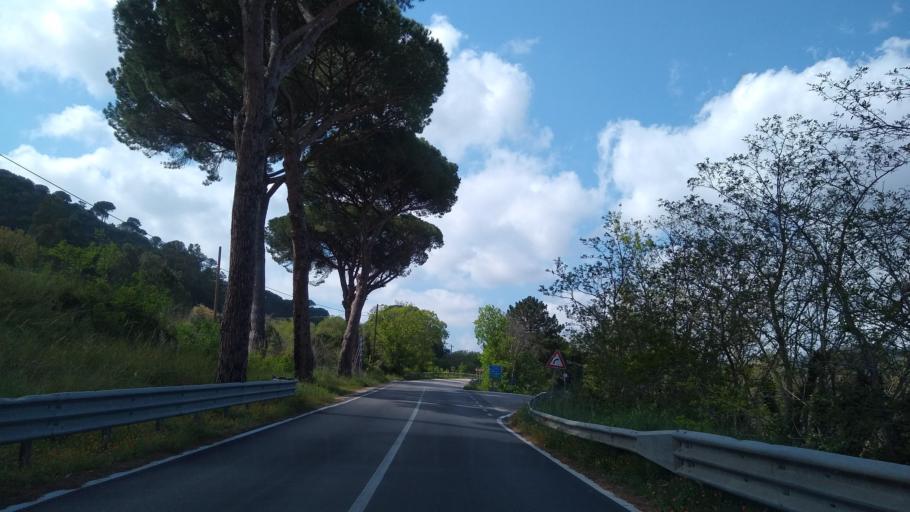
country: IT
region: Sicily
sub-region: Trapani
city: Calatafimi
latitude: 37.9363
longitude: 12.8537
